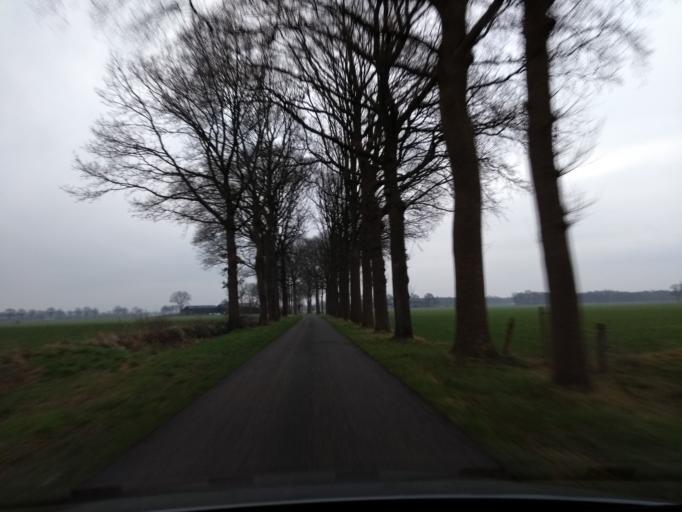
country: NL
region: Gelderland
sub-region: Gemeente Lochem
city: Harfsen
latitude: 52.2319
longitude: 6.3084
